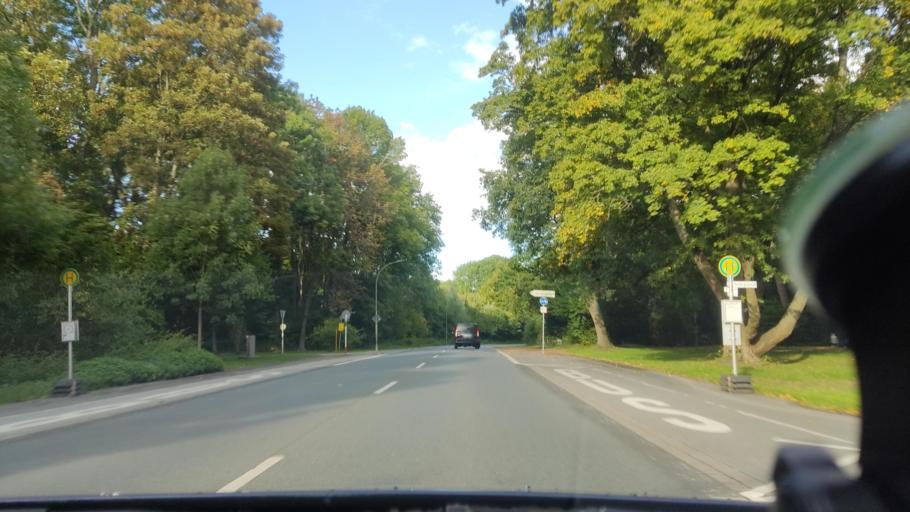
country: DE
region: North Rhine-Westphalia
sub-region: Regierungsbezirk Arnsberg
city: Dortmund
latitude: 51.5421
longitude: 7.4706
